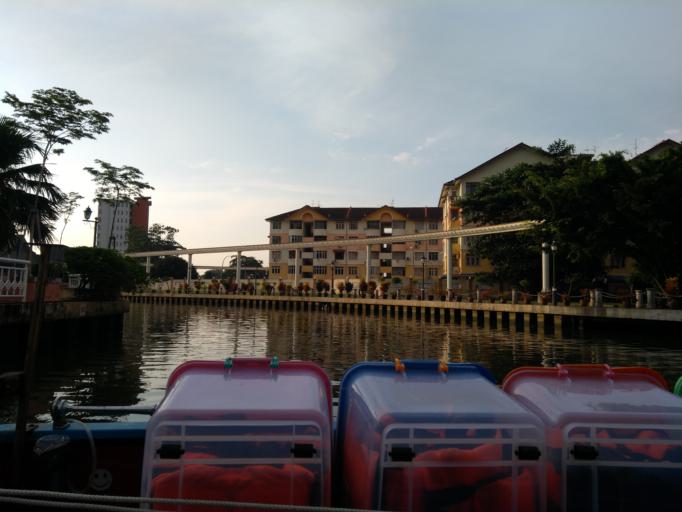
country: MY
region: Melaka
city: Malacca
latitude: 2.2055
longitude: 102.2511
